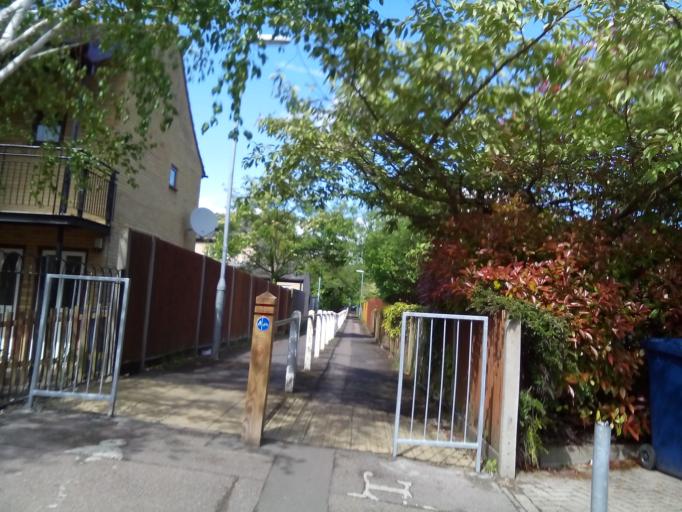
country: GB
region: England
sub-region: Cambridgeshire
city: Cambridge
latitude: 52.1840
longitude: 0.1620
